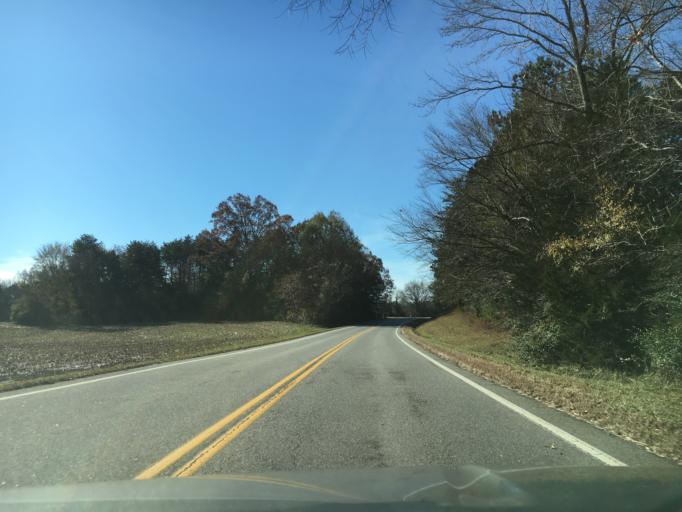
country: US
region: Virginia
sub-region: Cumberland County
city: Cumberland
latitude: 37.5300
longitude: -78.1996
